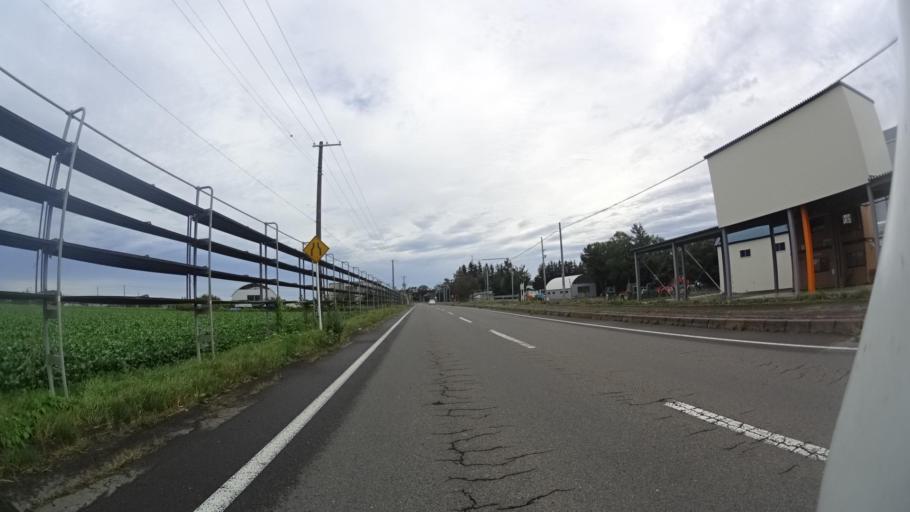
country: JP
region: Hokkaido
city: Abashiri
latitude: 43.8465
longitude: 144.5980
